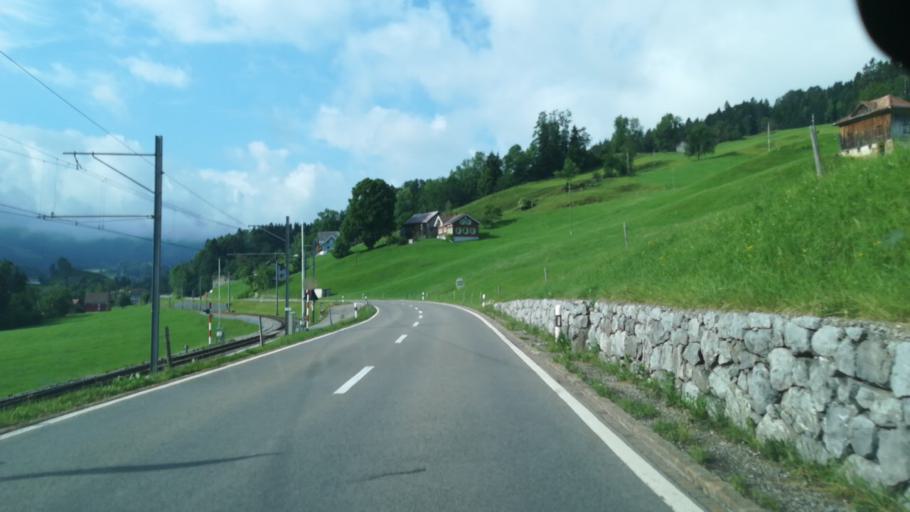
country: CH
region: Appenzell Ausserrhoden
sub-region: Bezirk Hinterland
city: Waldstatt
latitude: 47.3419
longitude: 9.2915
